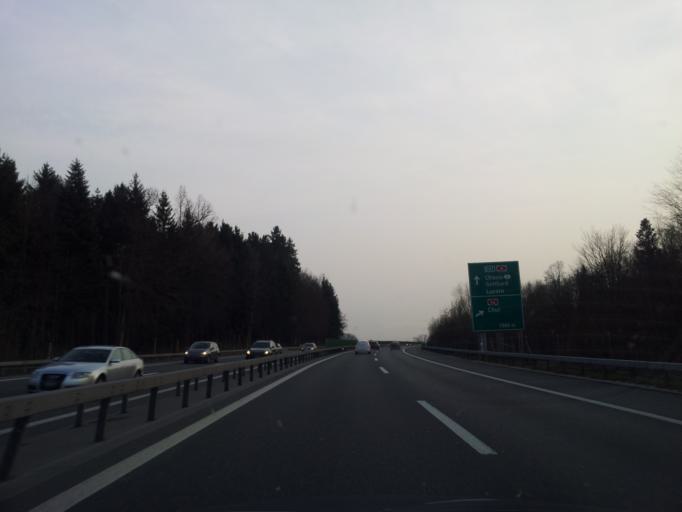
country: CH
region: Zurich
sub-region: Bezirk Affoltern
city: Knonau
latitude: 47.2124
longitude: 8.4710
